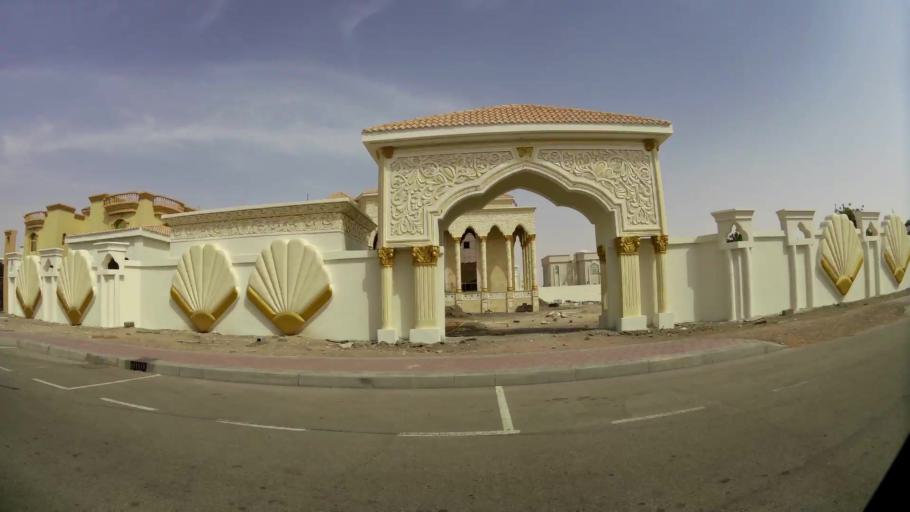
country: AE
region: Abu Dhabi
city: Al Ain
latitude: 24.1690
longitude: 55.6961
